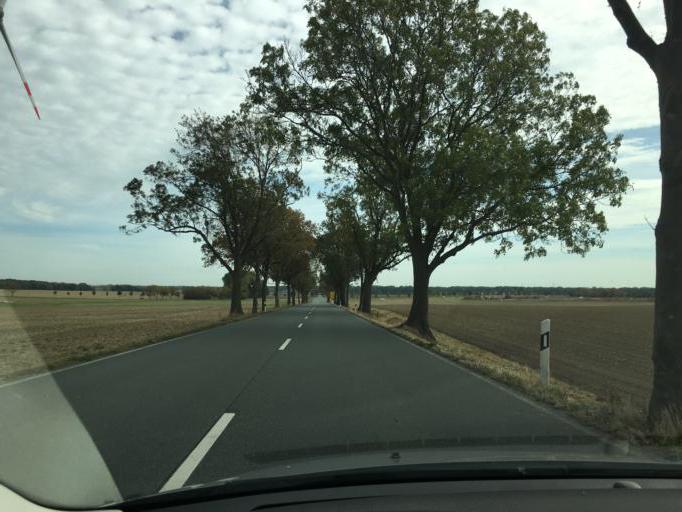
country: DE
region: Saxony
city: Stauchitz
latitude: 51.2746
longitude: 13.2139
